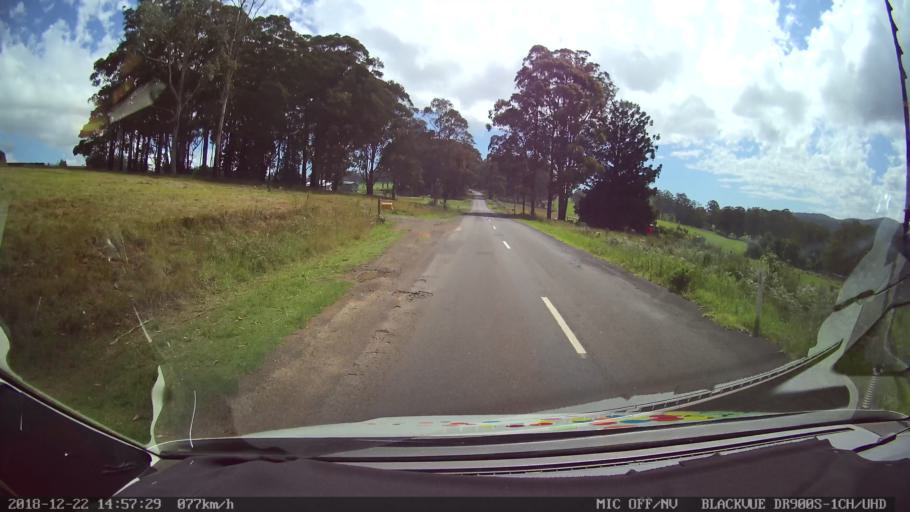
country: AU
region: New South Wales
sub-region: Bellingen
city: Dorrigo
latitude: -30.2345
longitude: 152.5008
